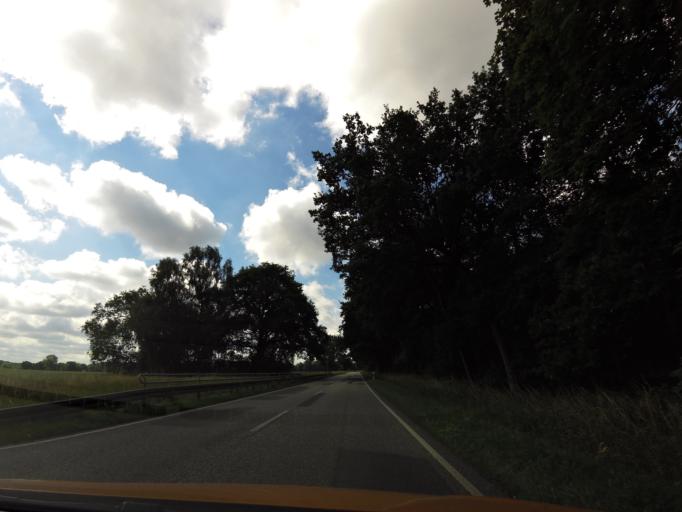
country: DE
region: Mecklenburg-Vorpommern
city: Plau am See
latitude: 53.5275
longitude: 12.2788
